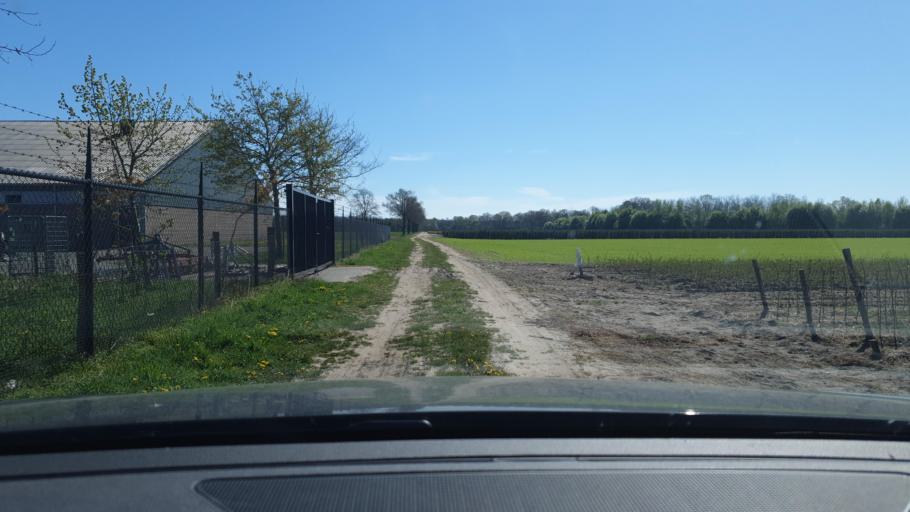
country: NL
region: Limburg
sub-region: Gemeente Venlo
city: Arcen
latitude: 51.4399
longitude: 6.1077
